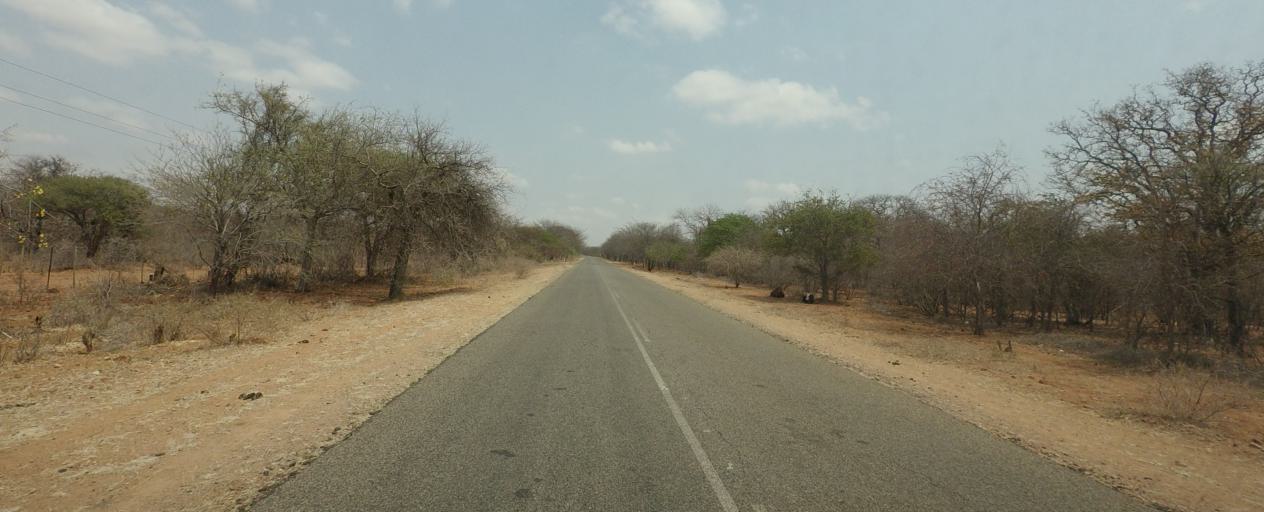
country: ZA
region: Limpopo
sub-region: Vhembe District Municipality
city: Mutale
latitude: -22.4212
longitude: 30.9341
